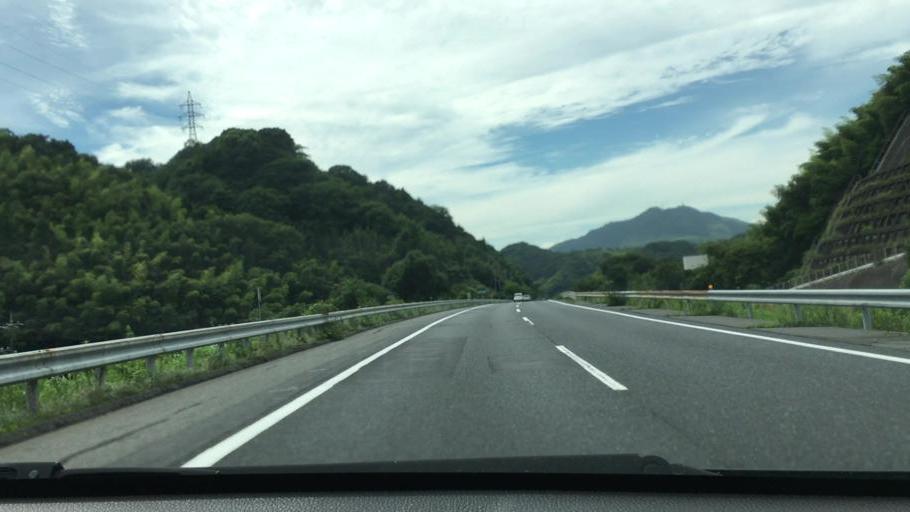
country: JP
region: Yamaguchi
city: Tokuyama
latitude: 34.0739
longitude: 131.8062
